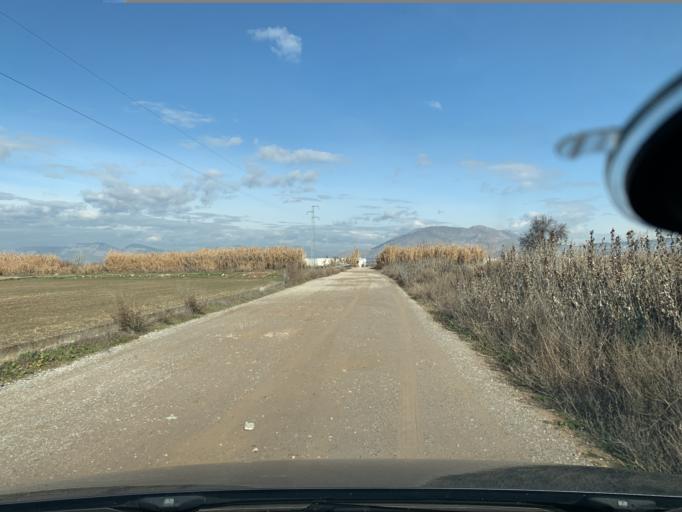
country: ES
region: Andalusia
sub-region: Provincia de Granada
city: Chauchina
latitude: 37.1838
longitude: -3.7498
